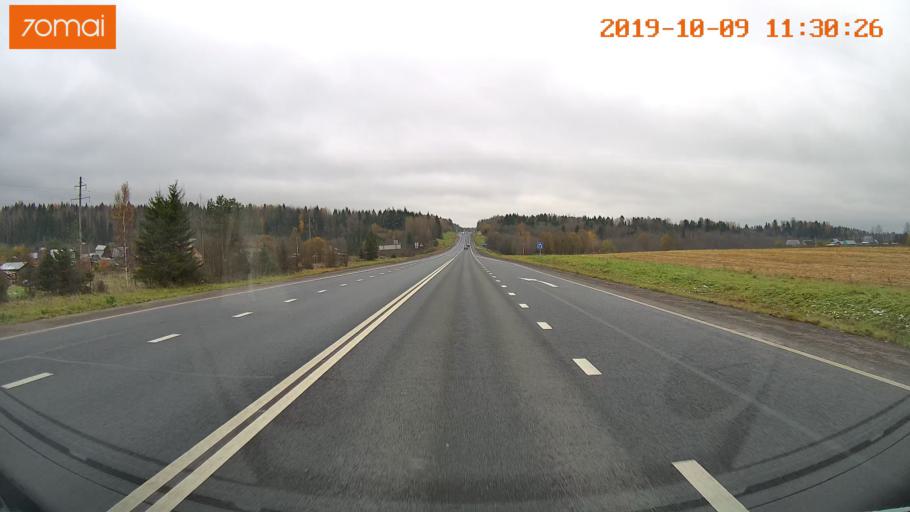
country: RU
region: Vologda
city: Gryazovets
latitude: 59.0538
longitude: 40.0751
